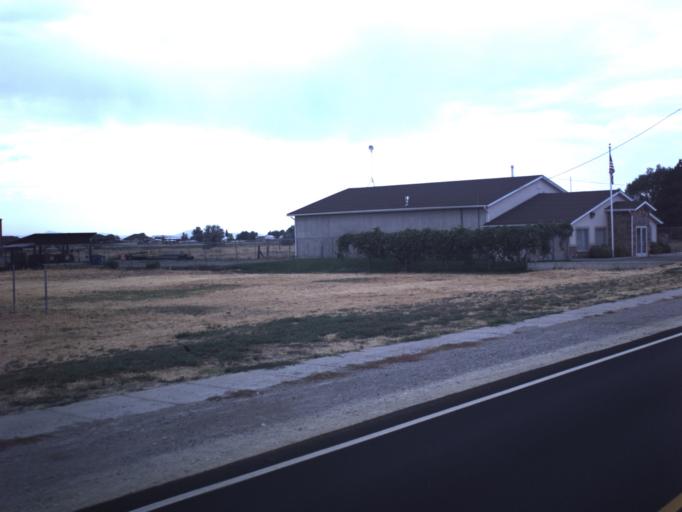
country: US
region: Utah
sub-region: Weber County
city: Hooper
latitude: 41.1639
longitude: -112.1132
